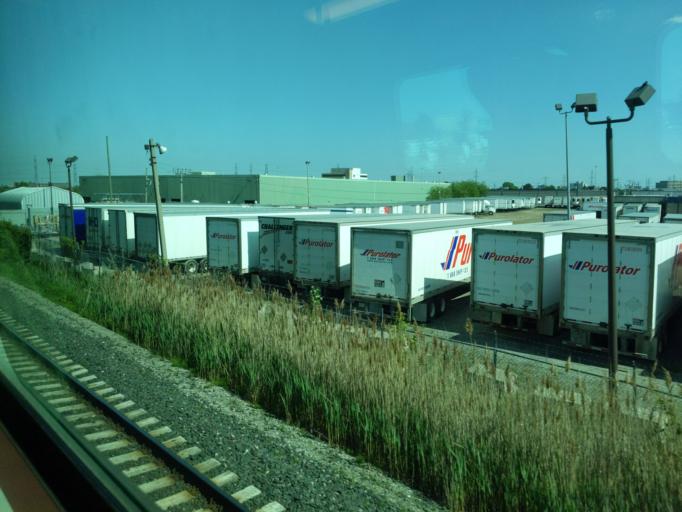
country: CA
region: Ontario
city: Etobicoke
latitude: 43.7061
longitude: -79.5751
